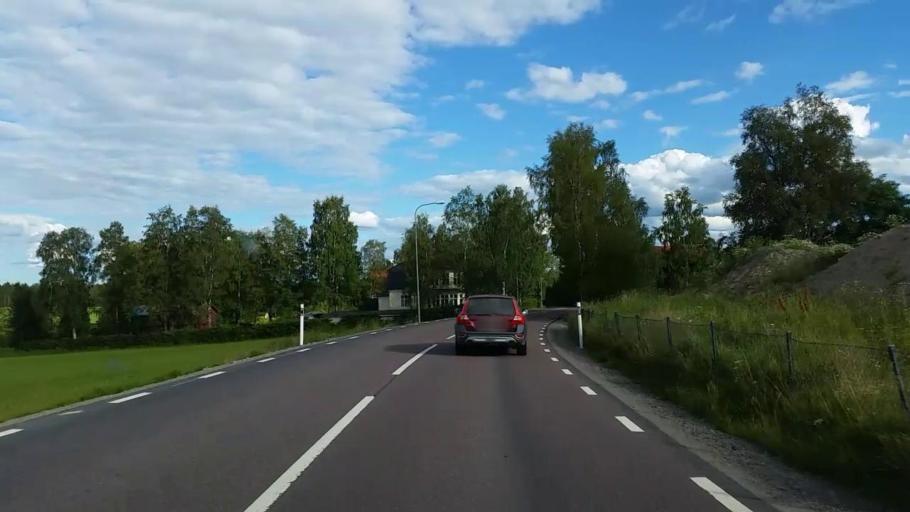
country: SE
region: Gaevleborg
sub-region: Ljusdals Kommun
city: Ljusdal
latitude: 61.8479
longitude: 15.9983
